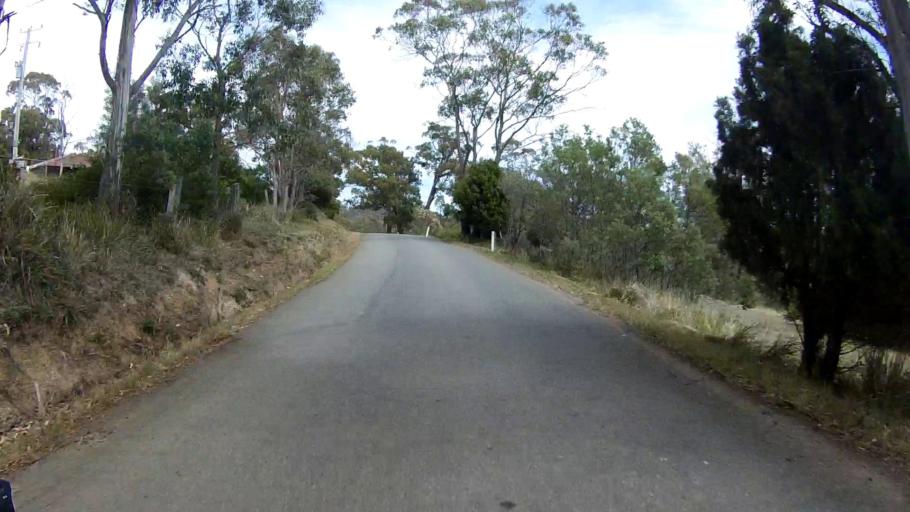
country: AU
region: Tasmania
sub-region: Sorell
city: Sorell
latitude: -42.7934
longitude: 147.6902
